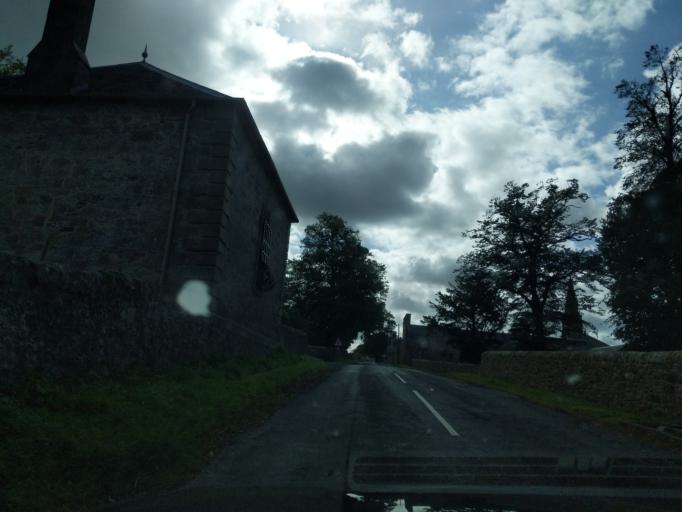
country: GB
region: Scotland
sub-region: Midlothian
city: Bonnyrigg
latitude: 55.8061
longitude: -3.1122
